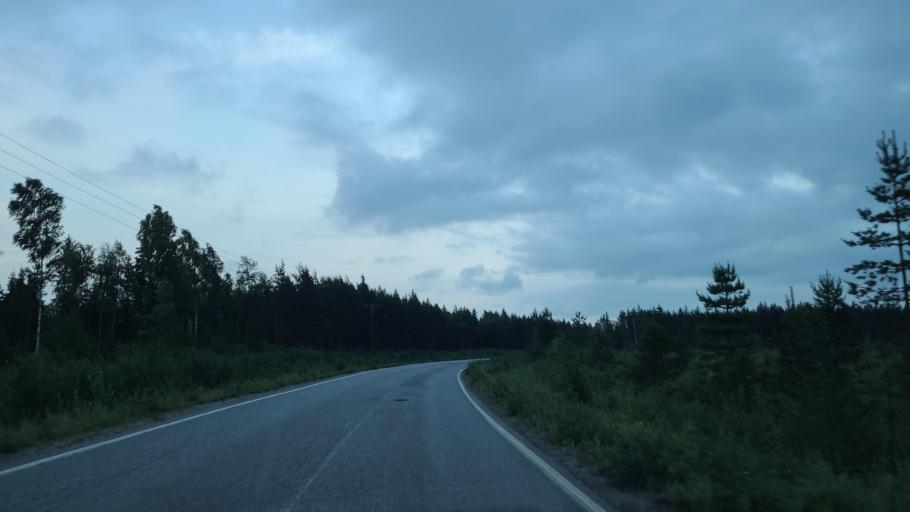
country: FI
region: Ostrobothnia
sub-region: Vaasa
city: Replot
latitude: 63.2226
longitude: 21.2425
